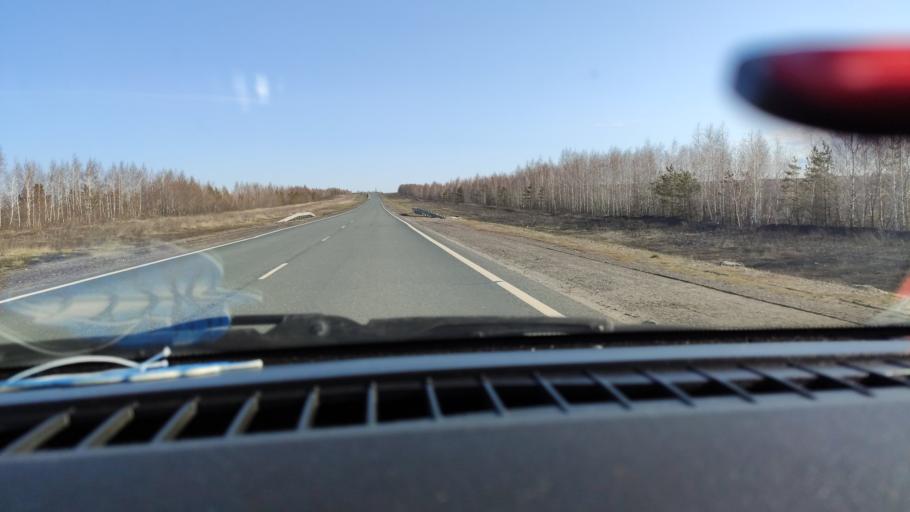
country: RU
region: Saratov
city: Dukhovnitskoye
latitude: 52.8266
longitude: 48.2370
